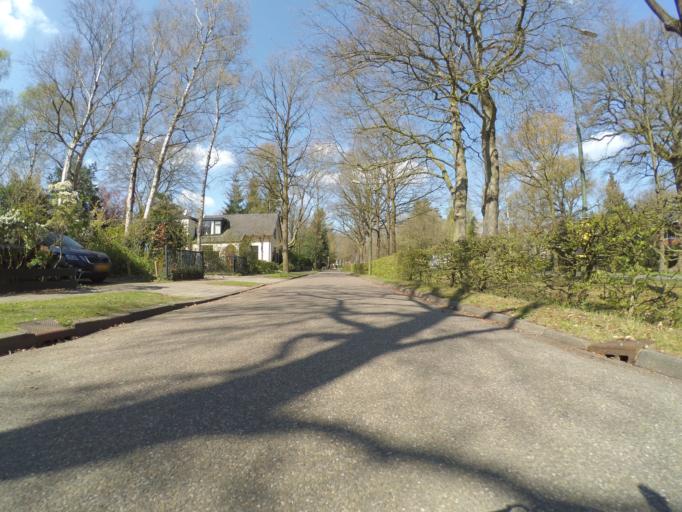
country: NL
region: Utrecht
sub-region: Gemeente Utrechtse Heuvelrug
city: Driebergen-Rijsenburg
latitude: 52.0490
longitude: 5.2922
